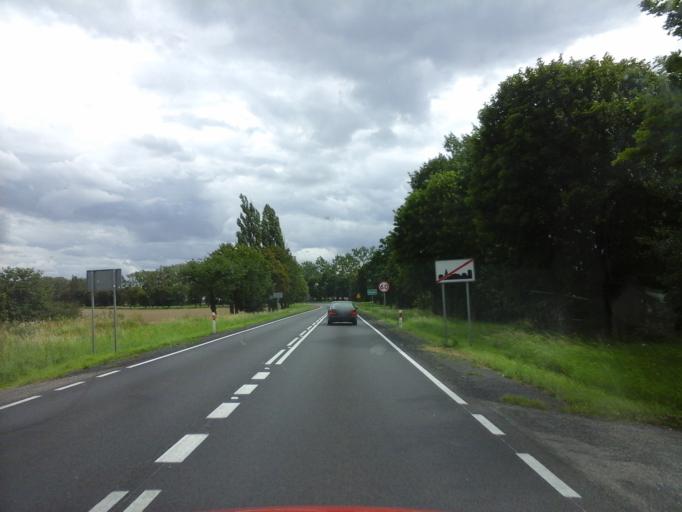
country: PL
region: West Pomeranian Voivodeship
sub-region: Powiat stargardzki
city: Dolice
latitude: 53.2977
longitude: 15.1808
